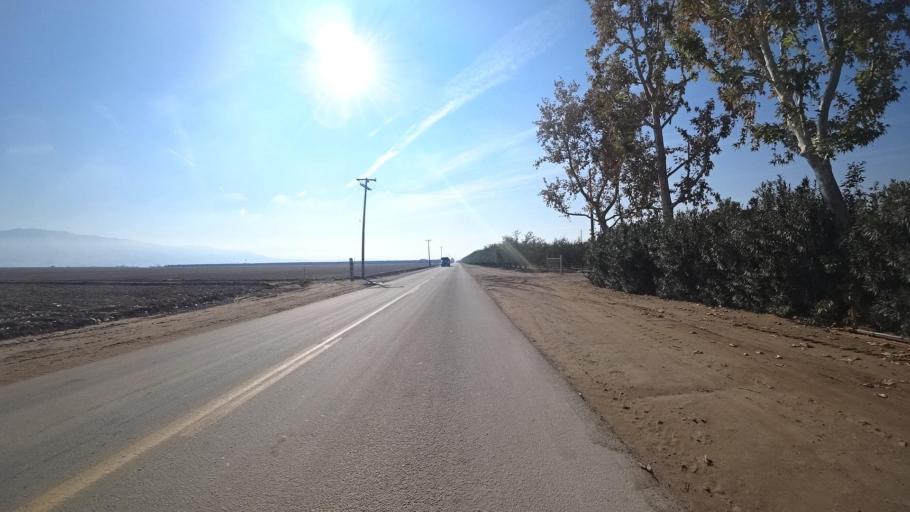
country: US
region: California
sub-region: Kern County
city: Arvin
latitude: 35.2457
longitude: -118.8605
